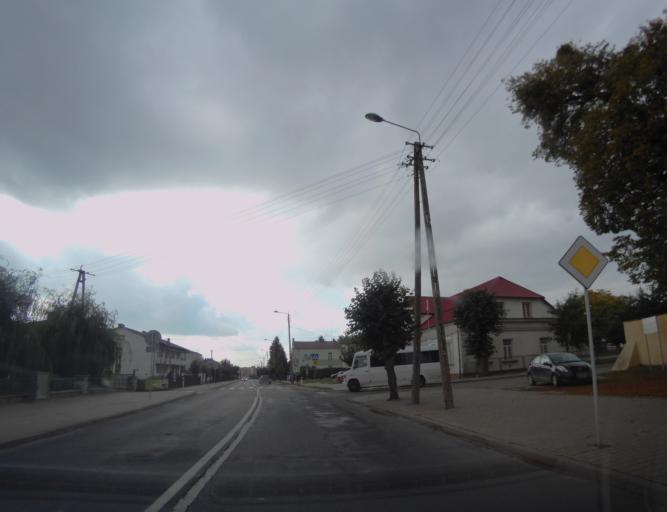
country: PL
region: Lublin Voivodeship
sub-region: Powiat krasnostawski
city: Zolkiewka
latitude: 50.9121
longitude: 22.8403
